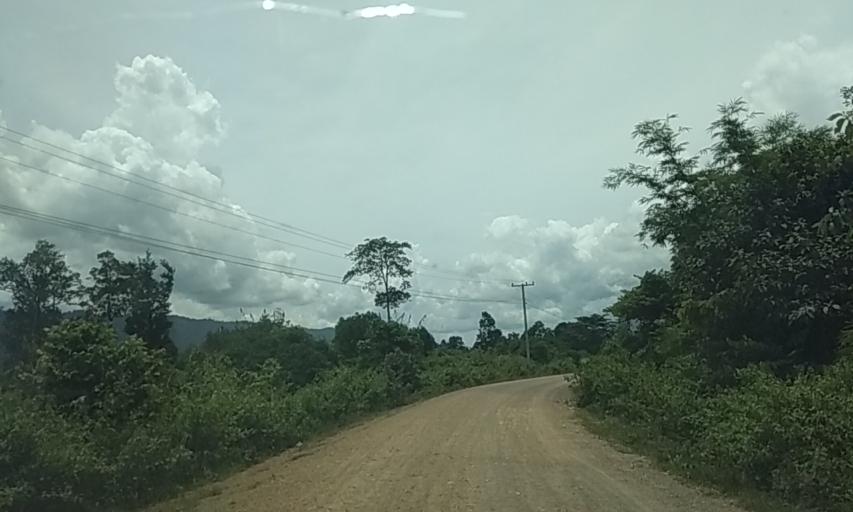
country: LA
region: Bolikhamxai
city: Ban Nahin
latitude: 18.1433
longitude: 104.7560
